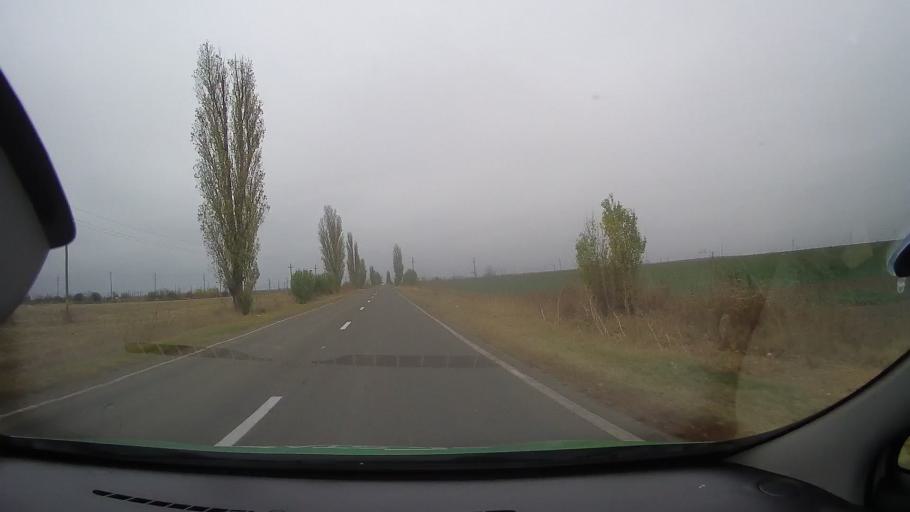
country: RO
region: Ialomita
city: Tandarei
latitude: 44.6595
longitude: 27.6463
